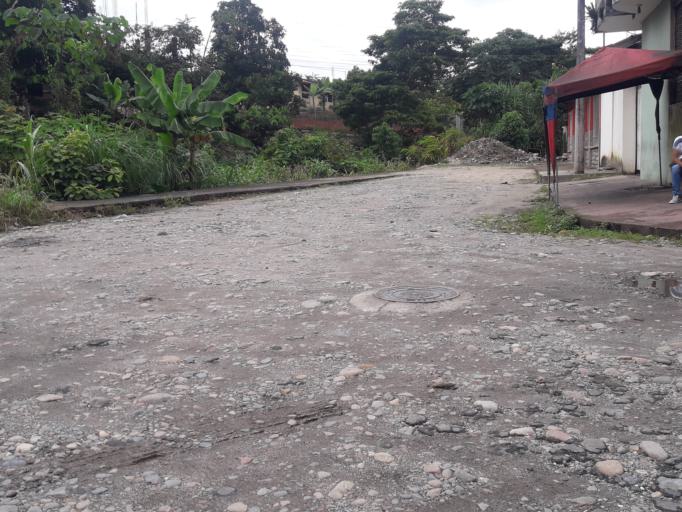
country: EC
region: Napo
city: Tena
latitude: -1.0005
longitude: -77.8104
